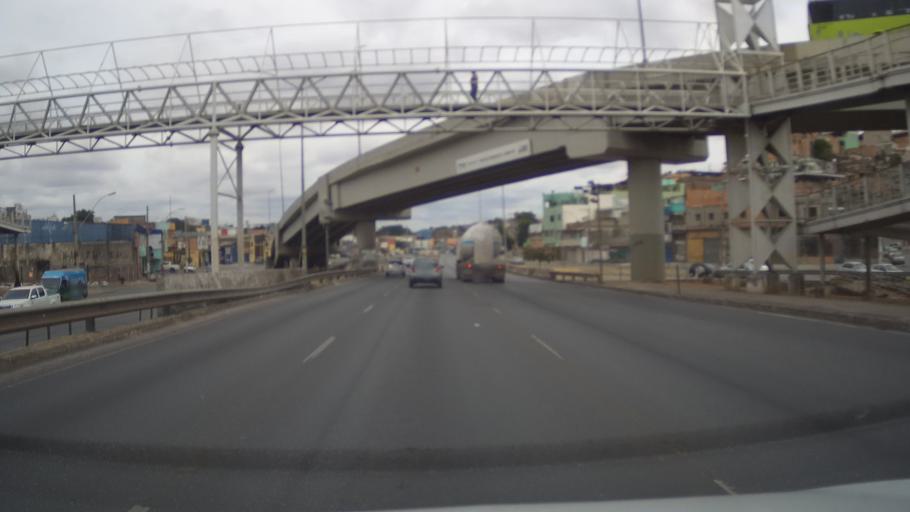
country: BR
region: Minas Gerais
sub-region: Belo Horizonte
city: Belo Horizonte
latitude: -19.8642
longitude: -43.9312
